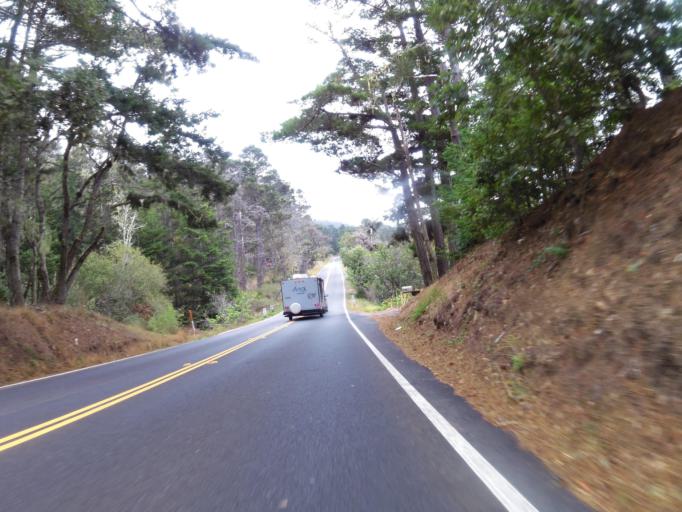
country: US
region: California
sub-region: Sonoma County
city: Sea Ranch
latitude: 38.5415
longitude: -123.2871
